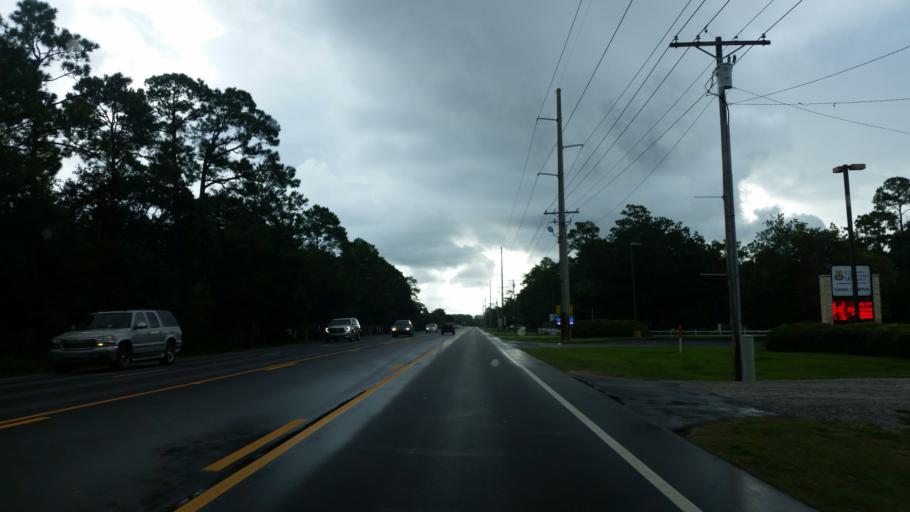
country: US
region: Alabama
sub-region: Baldwin County
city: Orange Beach
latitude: 30.2903
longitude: -87.5933
